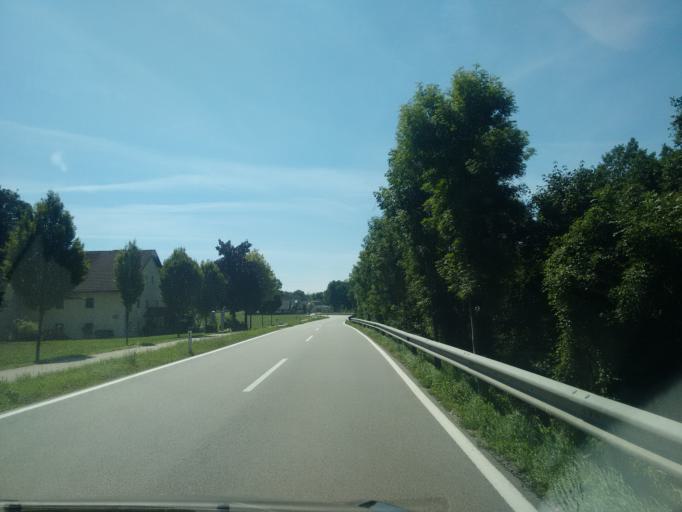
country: DE
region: Bavaria
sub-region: Lower Bavaria
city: Kirchdorf am Inn
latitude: 48.2279
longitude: 13.0059
